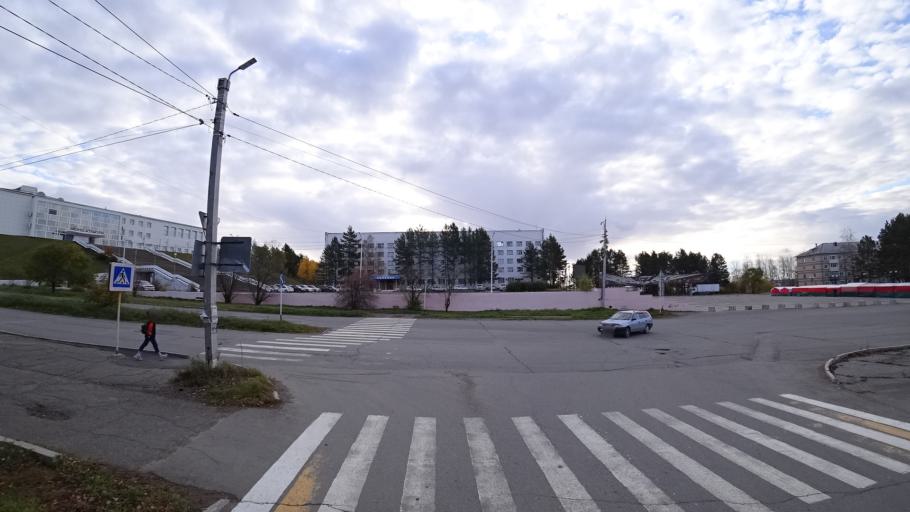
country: RU
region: Khabarovsk Krai
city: Amursk
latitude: 50.2273
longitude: 136.9099
